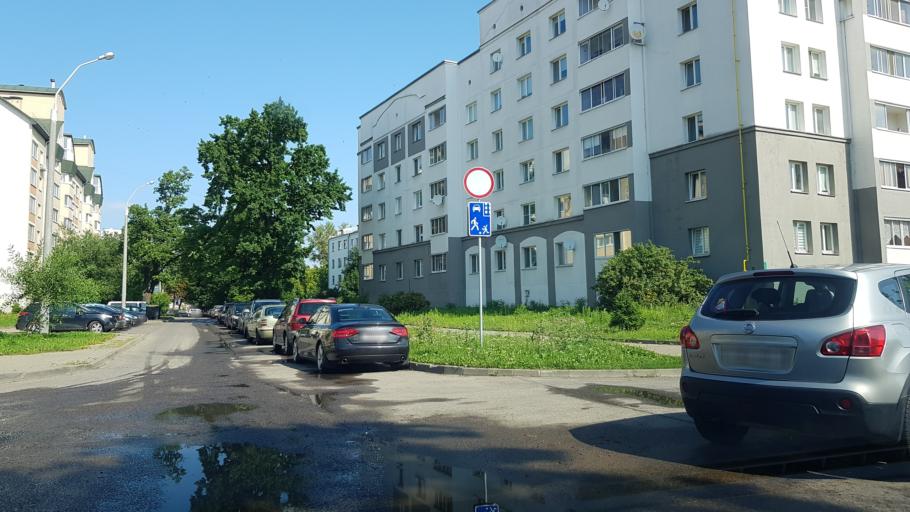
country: BY
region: Minsk
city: Minsk
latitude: 53.8861
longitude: 27.5283
